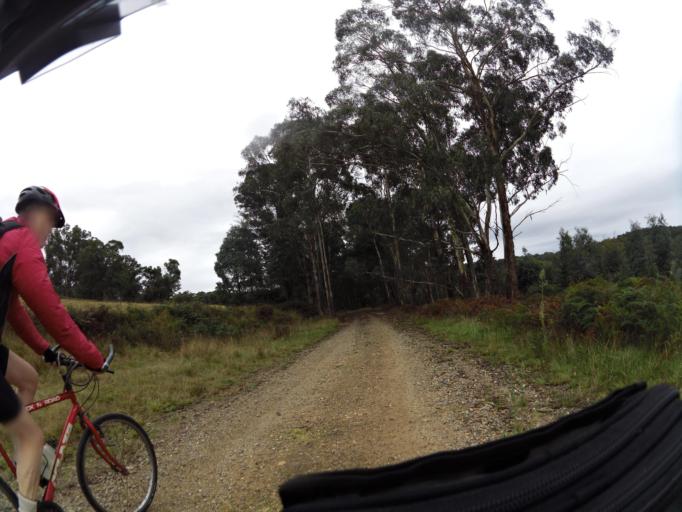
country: AU
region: New South Wales
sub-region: Greater Hume Shire
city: Holbrook
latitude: -36.1490
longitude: 147.4716
